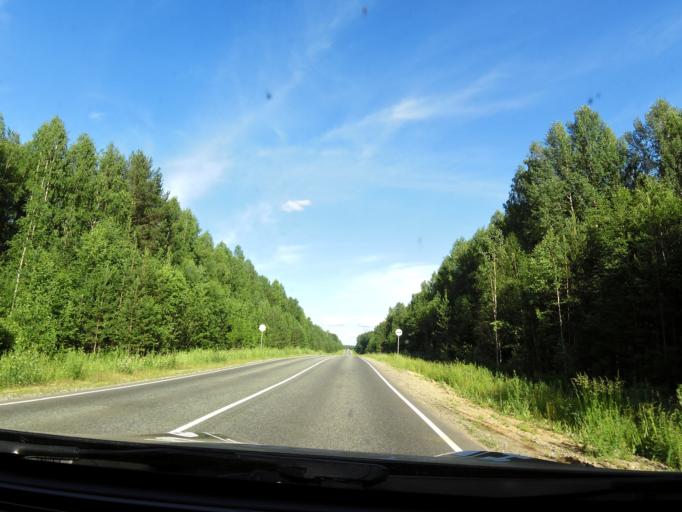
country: RU
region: Kirov
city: Chernaya Kholunitsa
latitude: 58.8627
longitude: 51.5974
